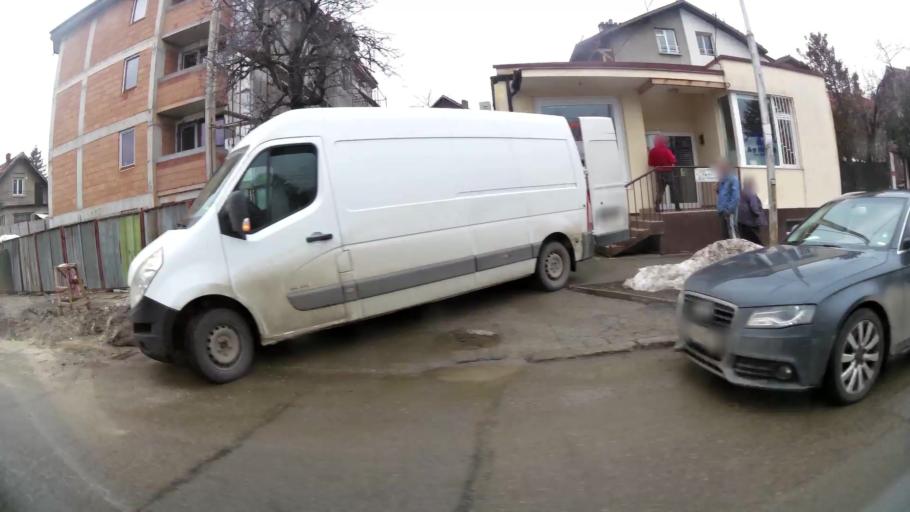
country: BG
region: Sofiya
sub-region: Obshtina Bozhurishte
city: Bozhurishte
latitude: 42.6734
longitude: 23.2402
